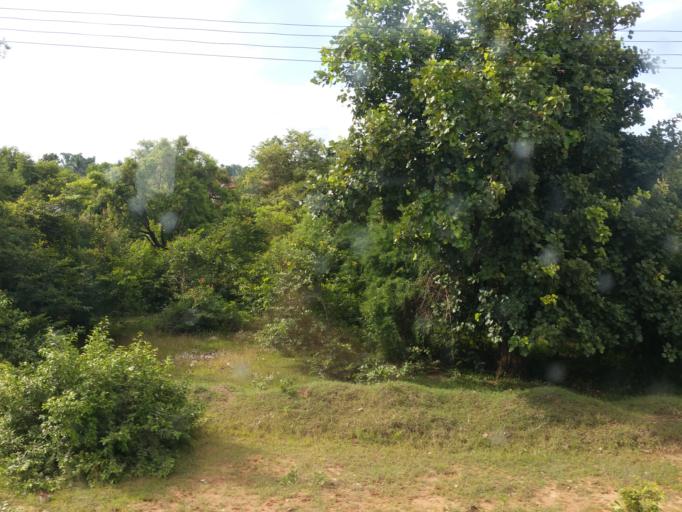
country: LA
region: Champasak
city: Pakxe
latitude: 15.0962
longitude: 105.7896
